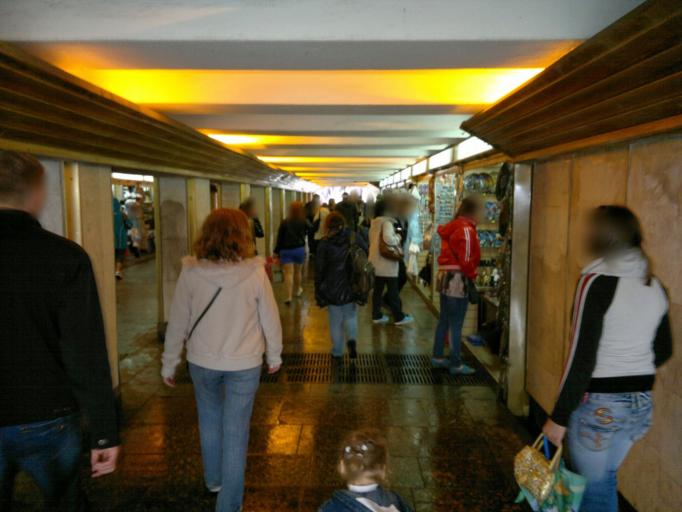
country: RU
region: St.-Petersburg
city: Saint Petersburg
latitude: 59.9344
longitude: 30.3355
